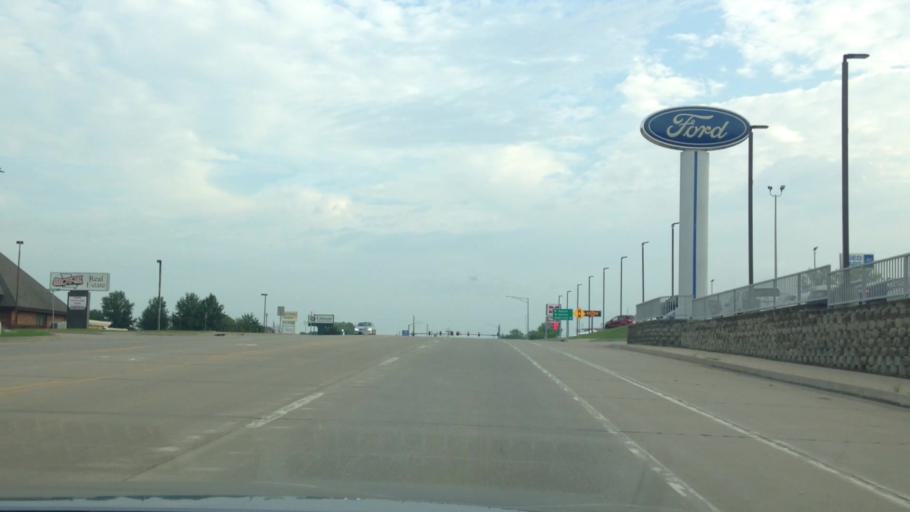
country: US
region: Missouri
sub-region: Clay County
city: Smithville
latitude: 39.3717
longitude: -94.5832
